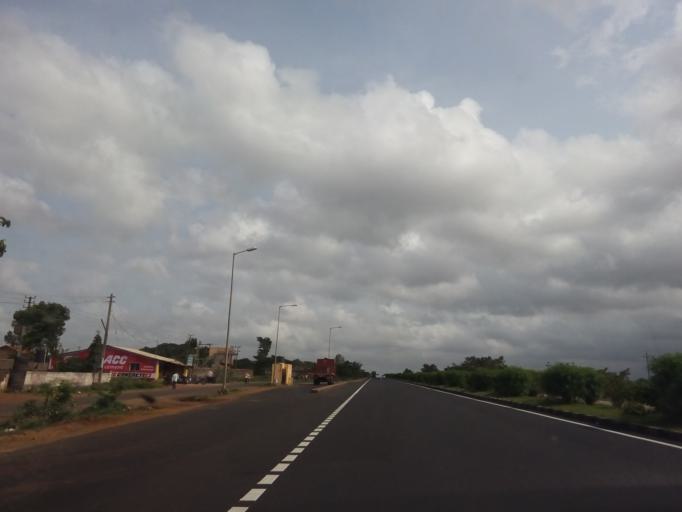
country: IN
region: Karnataka
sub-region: Belgaum
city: Hukeri
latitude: 16.1241
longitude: 74.5174
